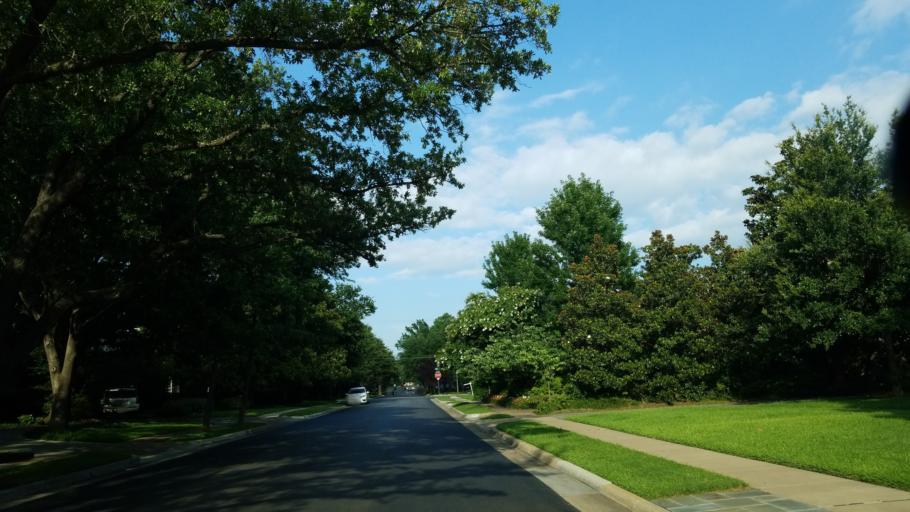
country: US
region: Texas
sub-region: Dallas County
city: Highland Park
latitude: 32.8400
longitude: -96.7967
